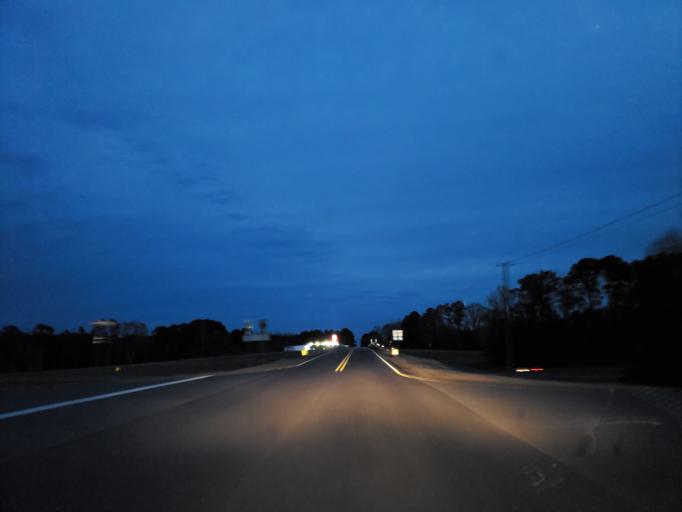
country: US
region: Alabama
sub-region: Greene County
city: Eutaw
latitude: 32.8695
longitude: -87.9256
